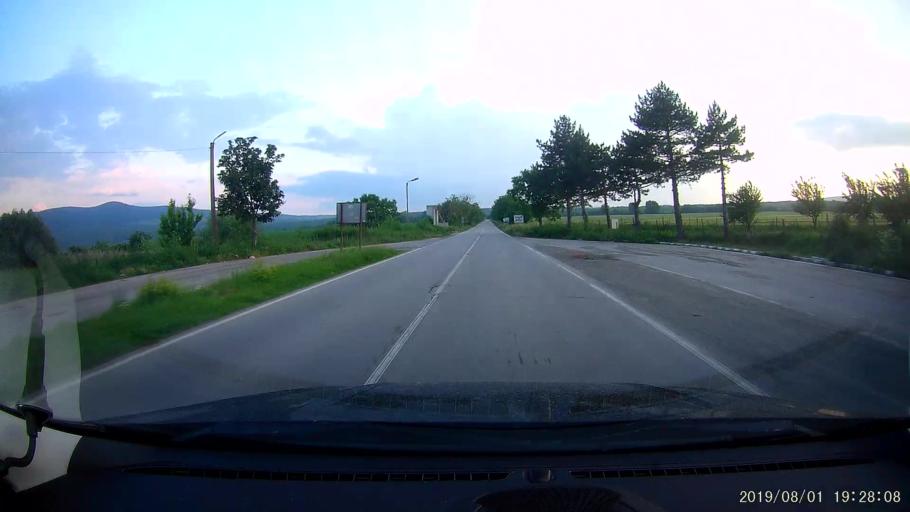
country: BG
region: Burgas
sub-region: Obshtina Sungurlare
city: Sungurlare
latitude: 42.8460
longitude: 26.9230
